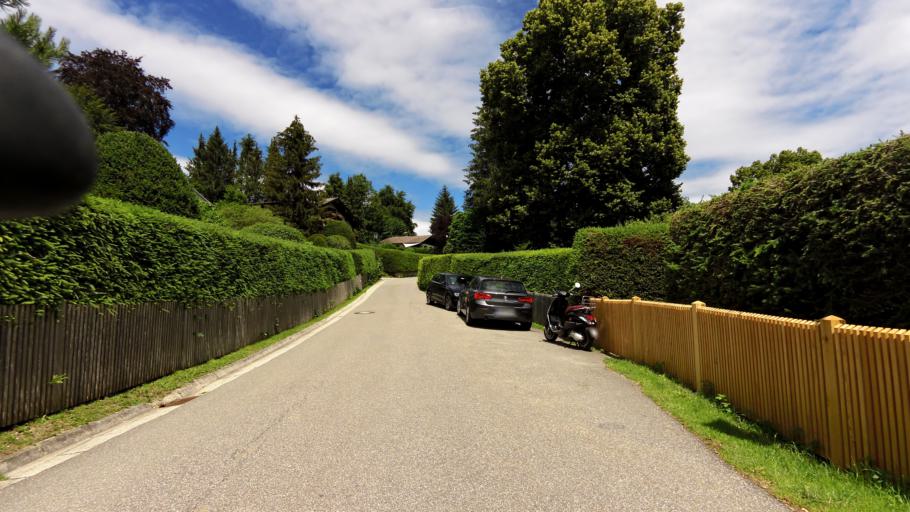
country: DE
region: Bavaria
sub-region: Upper Bavaria
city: Bad Wiessee
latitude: 47.6975
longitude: 11.7349
